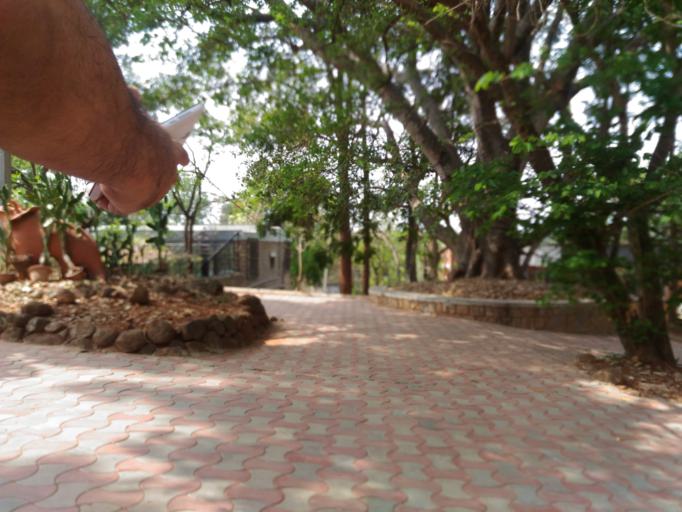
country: IN
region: Karnataka
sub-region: Bangalore Urban
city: Bangalore
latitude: 12.8533
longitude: 77.5103
